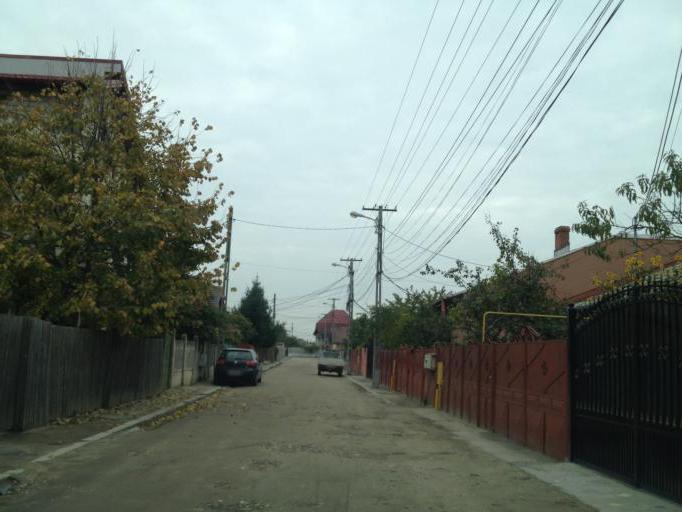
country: RO
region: Dolj
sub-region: Municipiul Craiova
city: Popoveni
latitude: 44.2931
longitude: 23.8048
